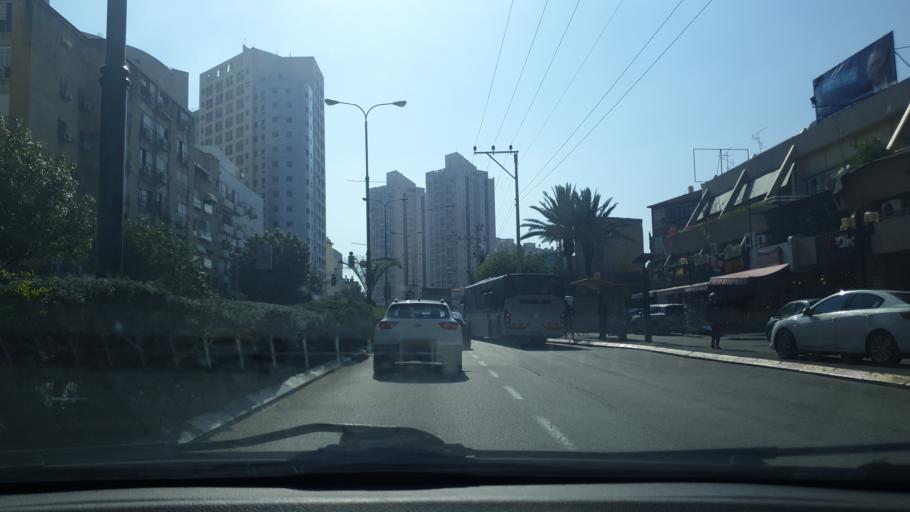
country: IL
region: Central District
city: Rishon LeZiyyon
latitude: 31.9689
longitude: 34.8042
